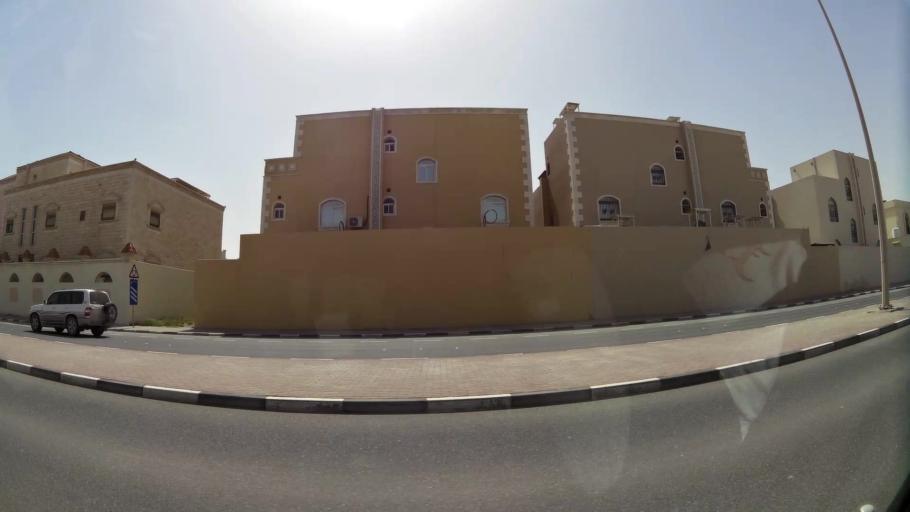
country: QA
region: Baladiyat Umm Salal
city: Umm Salal Muhammad
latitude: 25.3780
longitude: 51.4298
